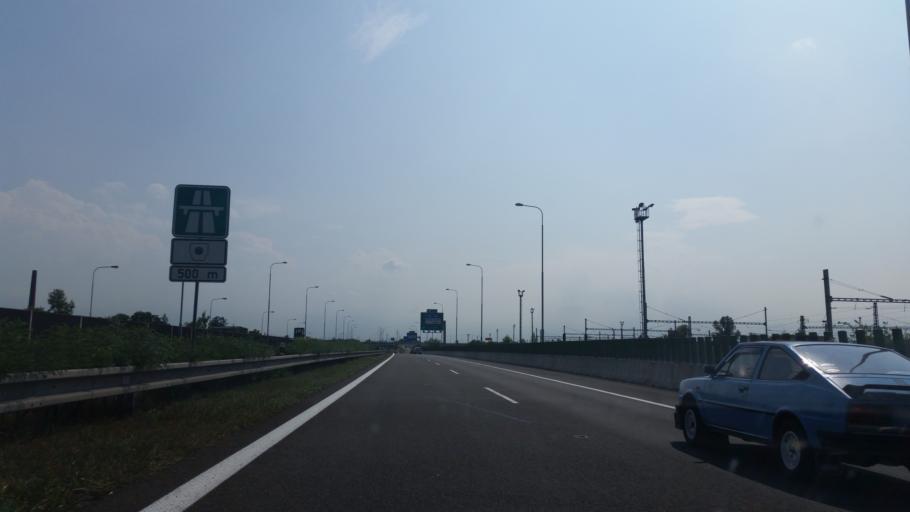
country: CZ
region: Moravskoslezsky
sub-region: Okres Ostrava-Mesto
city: Ostrava
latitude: 49.8177
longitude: 18.2097
